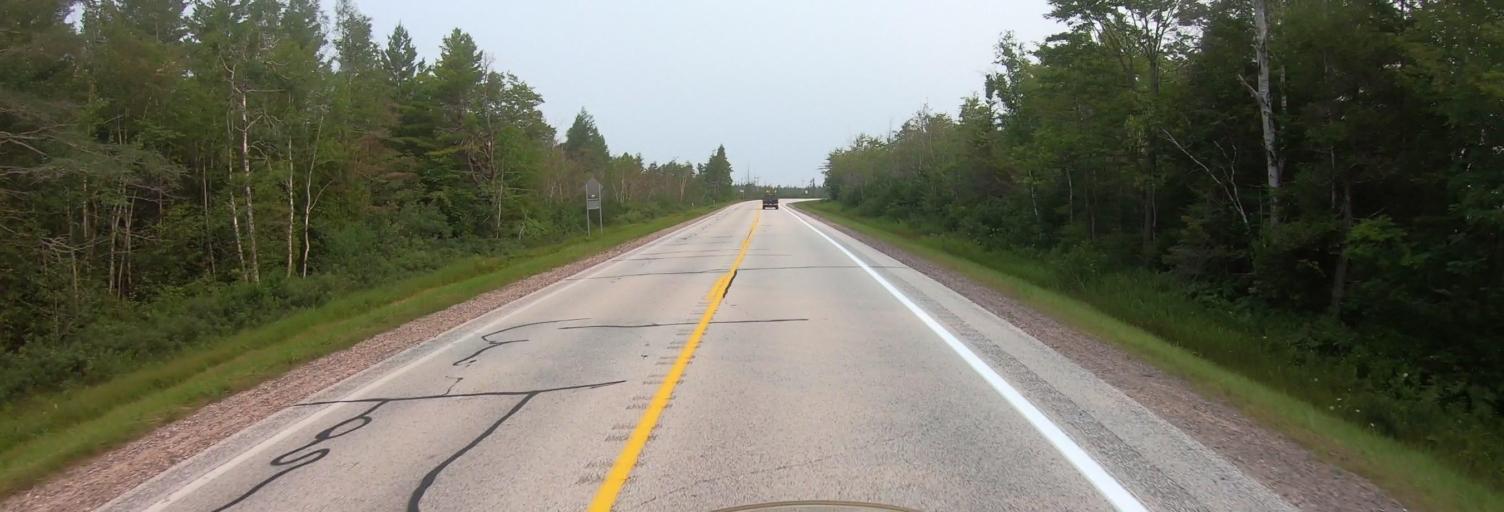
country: US
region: Michigan
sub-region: Luce County
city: Newberry
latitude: 46.5650
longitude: -85.0313
